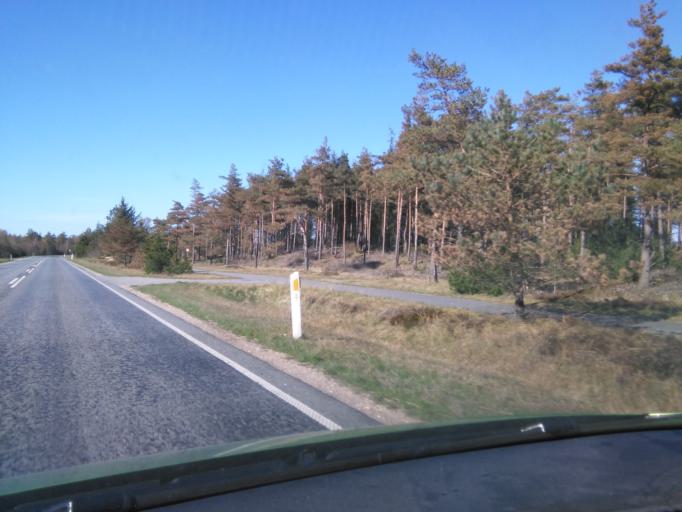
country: DK
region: South Denmark
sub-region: Varde Kommune
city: Oksbol
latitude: 55.5985
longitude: 8.2251
